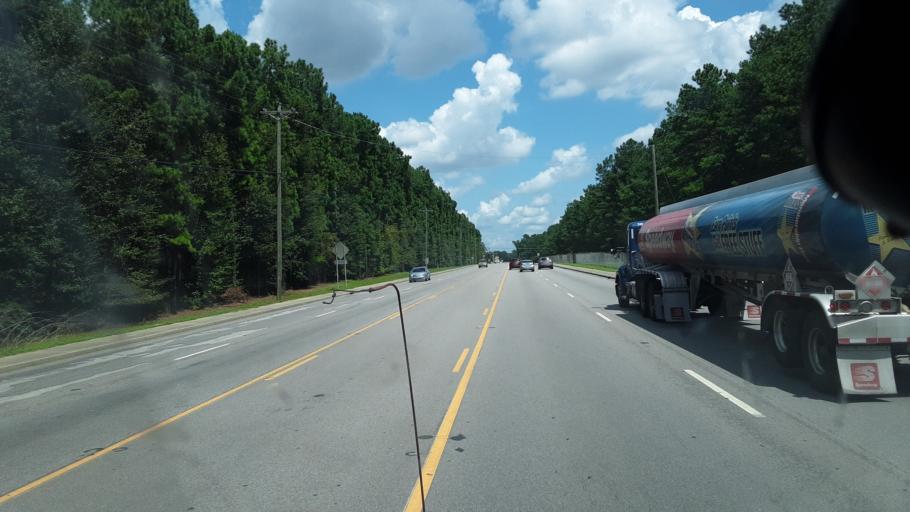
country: US
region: South Carolina
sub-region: Berkeley County
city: Sangaree
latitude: 33.0648
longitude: -80.0924
